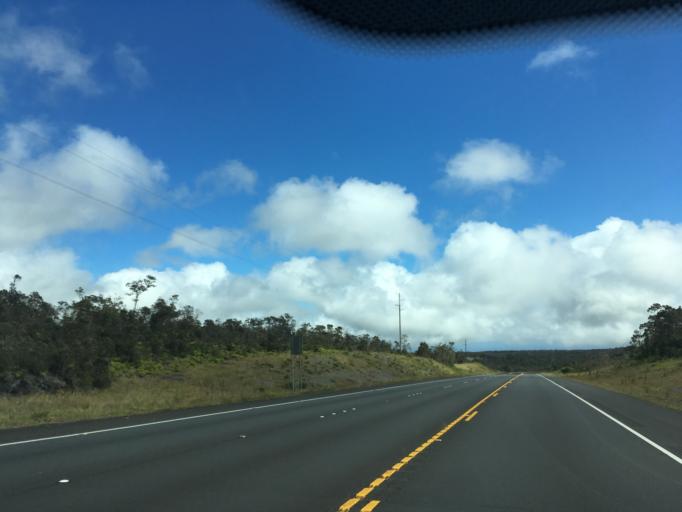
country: US
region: Hawaii
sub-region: Hawaii County
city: Wainaku
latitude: 19.6773
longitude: -155.3219
